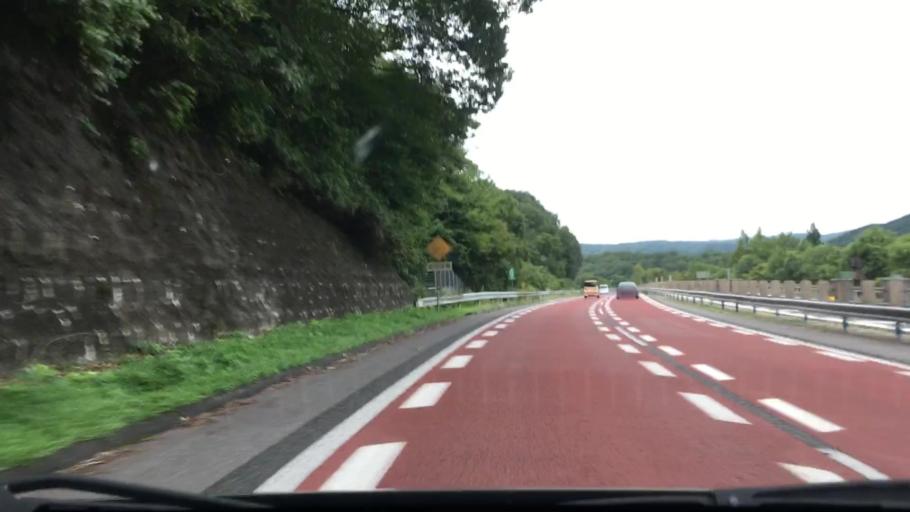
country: JP
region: Hiroshima
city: Miyoshi
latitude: 34.7787
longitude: 132.8425
